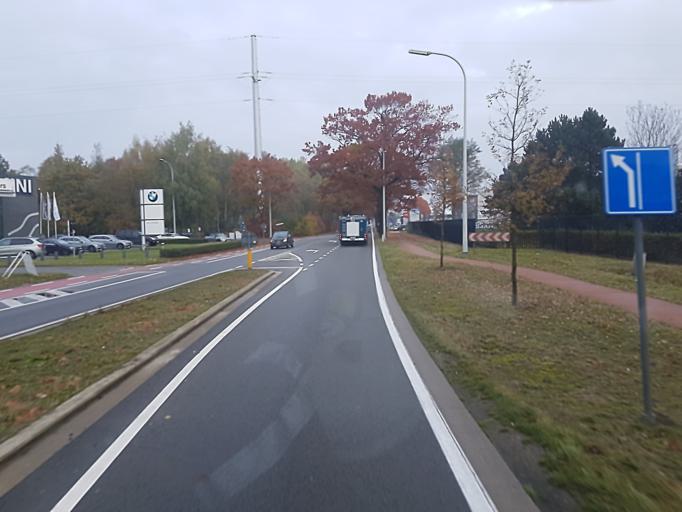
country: BE
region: Flanders
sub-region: Provincie Antwerpen
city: Vosselaar
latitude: 51.3035
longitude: 4.9174
